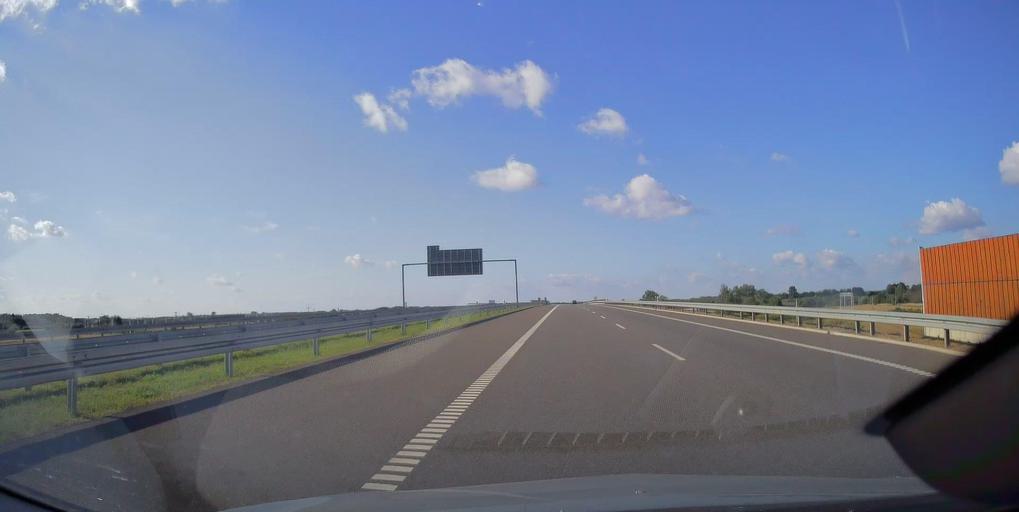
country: PL
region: Masovian Voivodeship
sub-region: Powiat szydlowiecki
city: Oronsko
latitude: 51.3498
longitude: 21.0150
